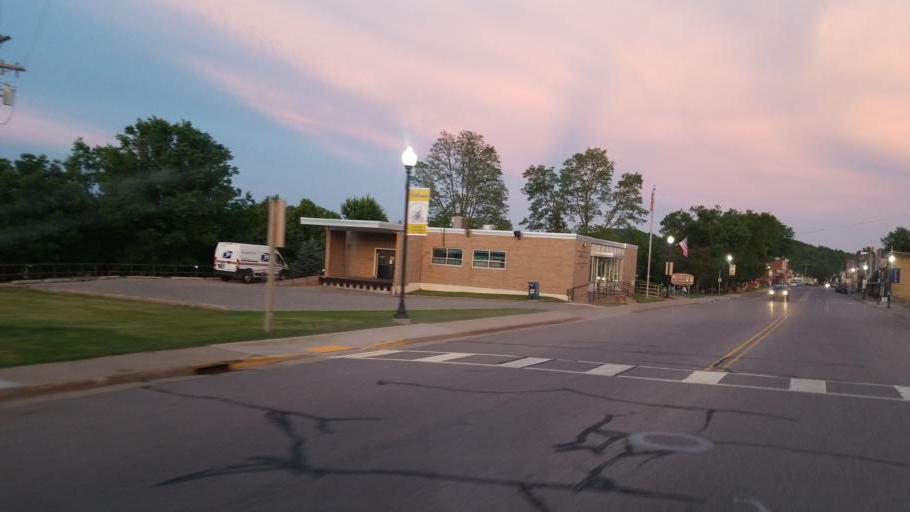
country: US
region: Wisconsin
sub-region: Juneau County
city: Elroy
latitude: 43.7400
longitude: -90.2716
